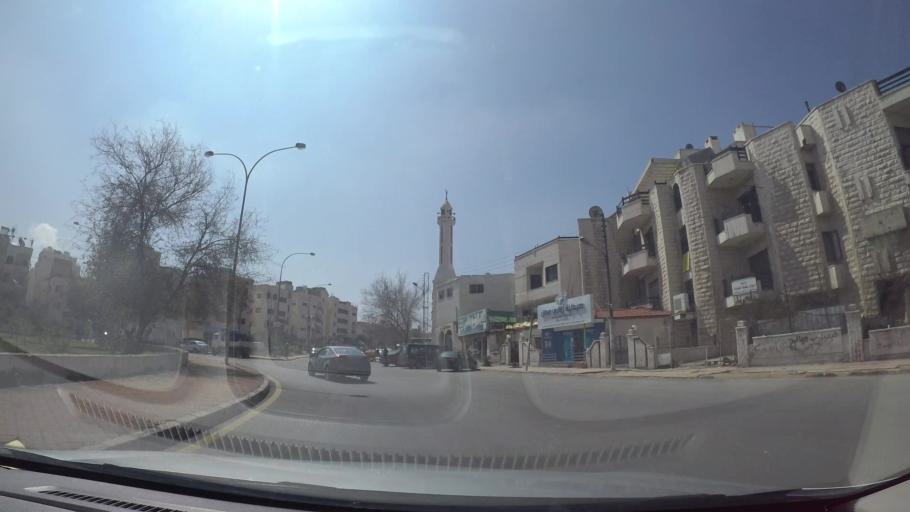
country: JO
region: Amman
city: Al Bunayyat ash Shamaliyah
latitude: 31.9301
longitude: 35.9035
